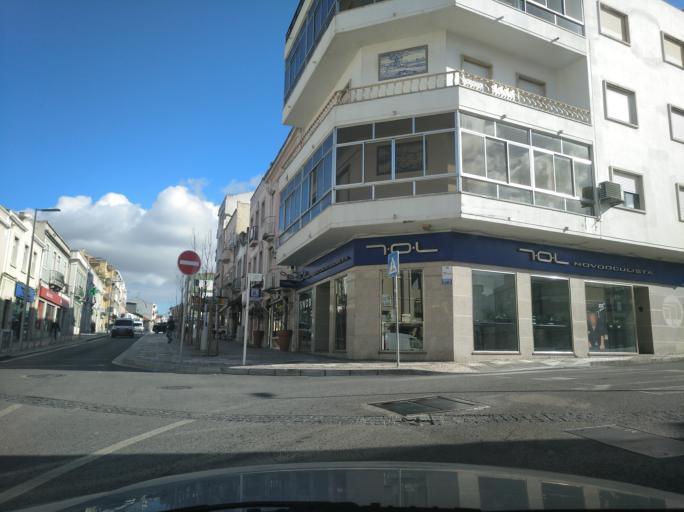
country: PT
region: Lisbon
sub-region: Loures
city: Loures
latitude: 38.8315
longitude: -9.1693
